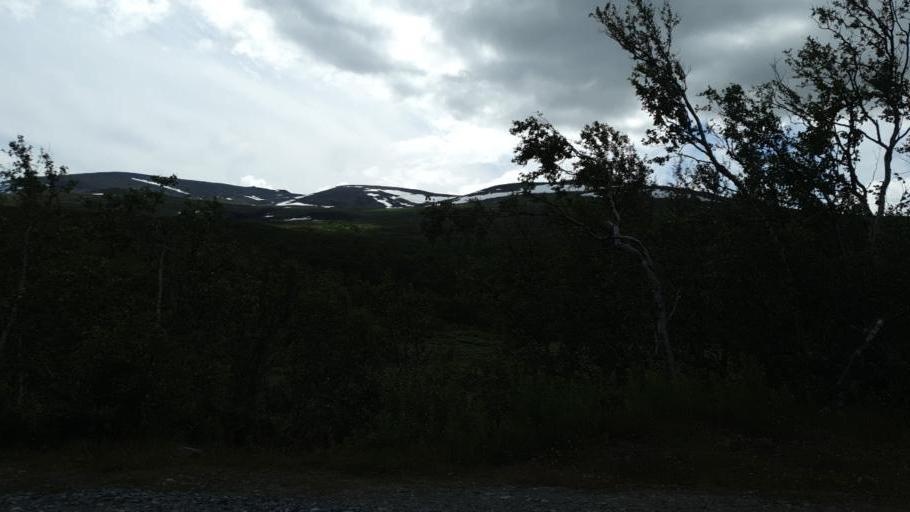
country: NO
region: Oppland
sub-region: Oystre Slidre
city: Heggenes
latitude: 61.4877
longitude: 8.8409
